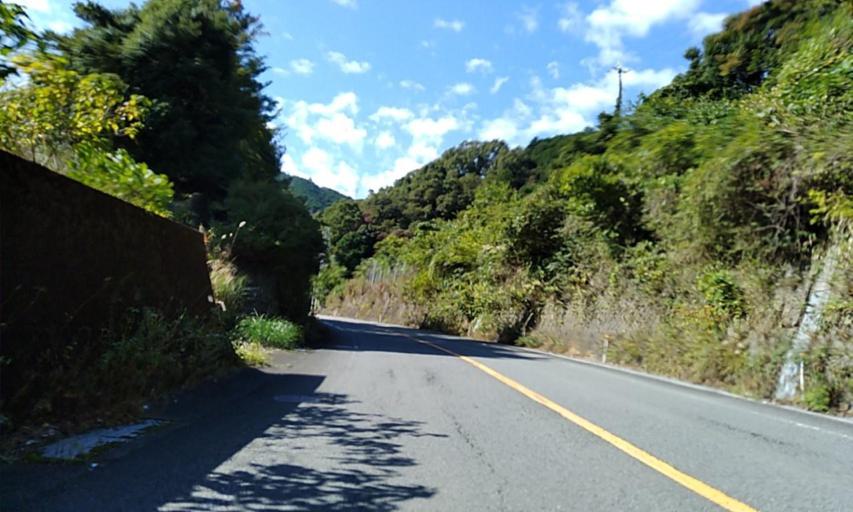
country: JP
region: Wakayama
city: Gobo
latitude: 33.9917
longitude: 135.1837
